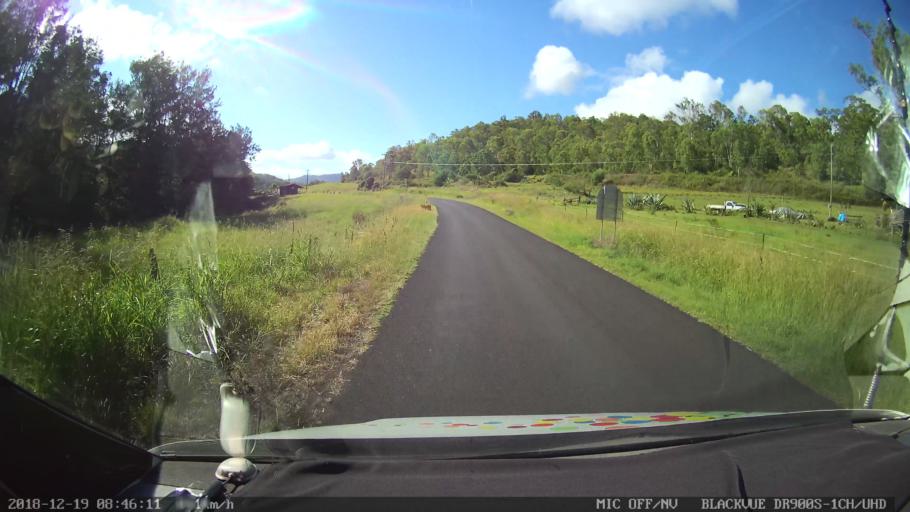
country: AU
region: New South Wales
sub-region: Kyogle
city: Kyogle
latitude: -28.3601
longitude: 152.9677
